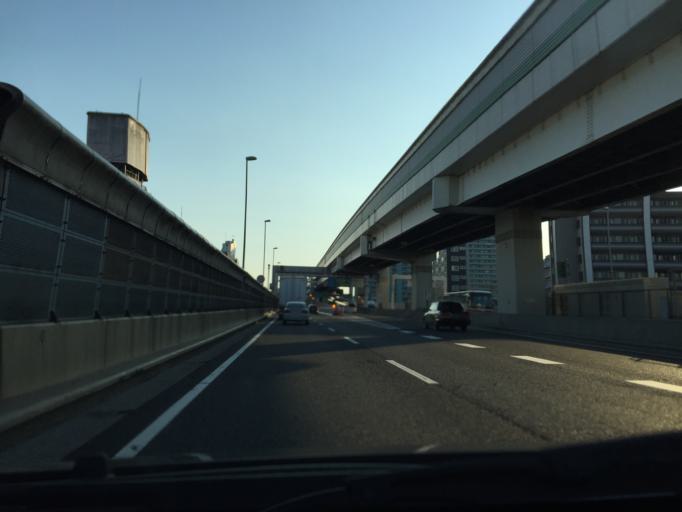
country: JP
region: Kanagawa
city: Yokohama
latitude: 35.4405
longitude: 139.6474
